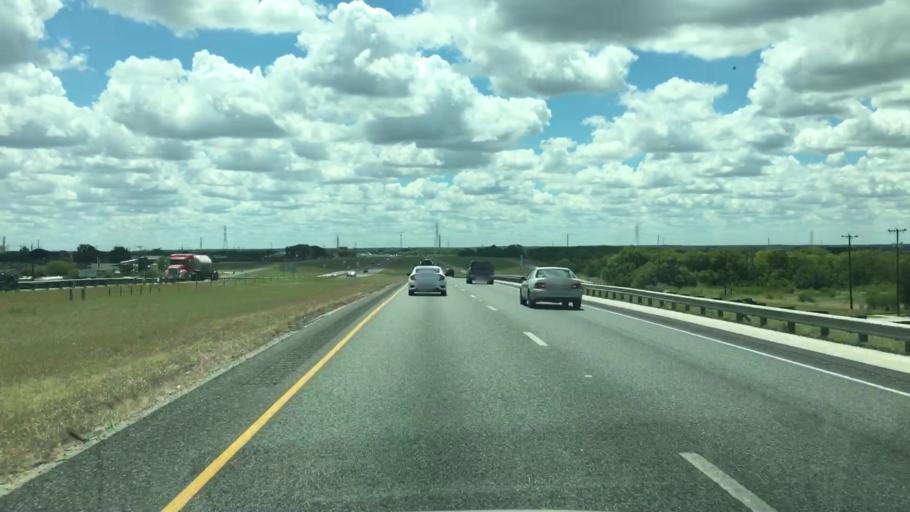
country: US
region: Texas
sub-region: Bexar County
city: Elmendorf
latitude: 29.2814
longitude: -98.3959
